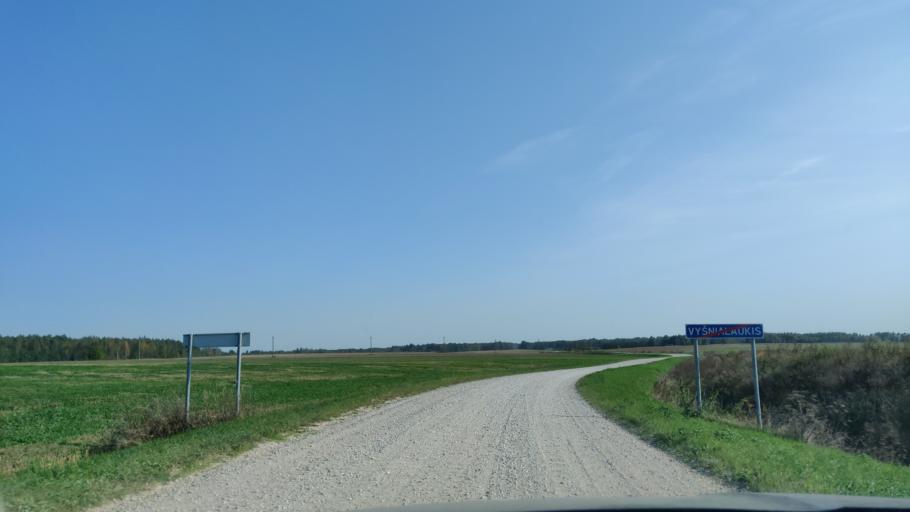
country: LT
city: Sirvintos
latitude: 54.9697
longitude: 24.8405
